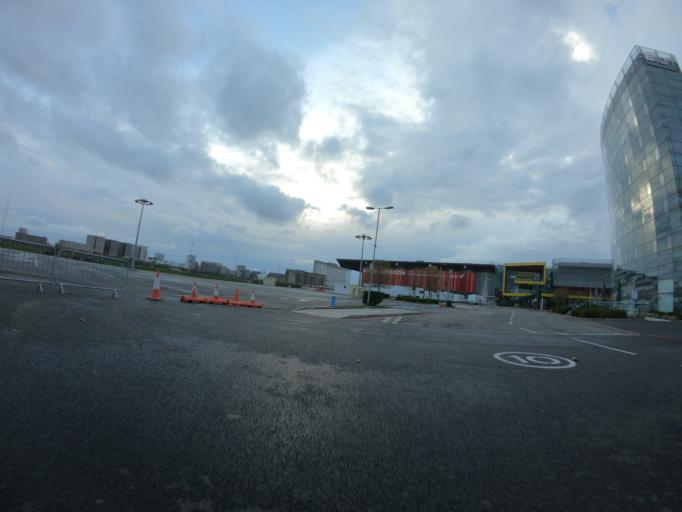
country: GB
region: England
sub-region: Greater London
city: East Ham
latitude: 51.5080
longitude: 0.0366
